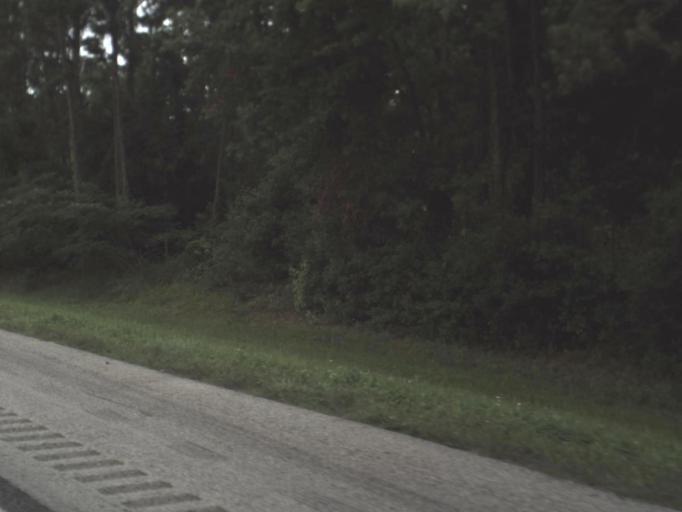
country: US
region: Florida
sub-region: Alachua County
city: Gainesville
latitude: 29.5209
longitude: -82.3088
